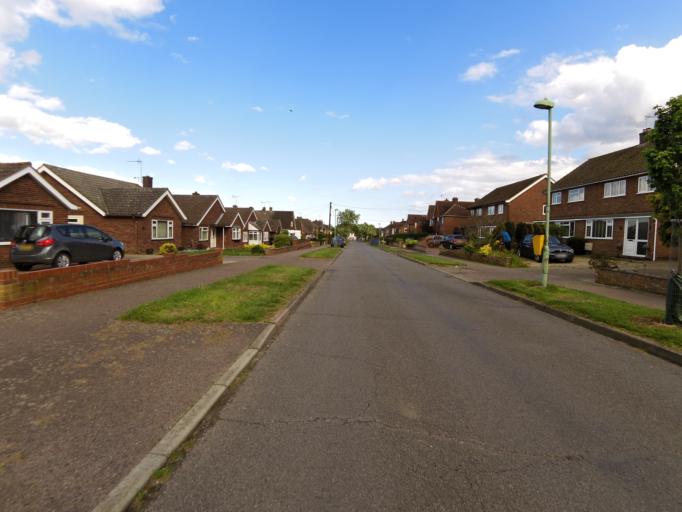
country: GB
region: England
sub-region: Suffolk
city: Stowmarket
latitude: 52.1913
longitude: 0.9815
